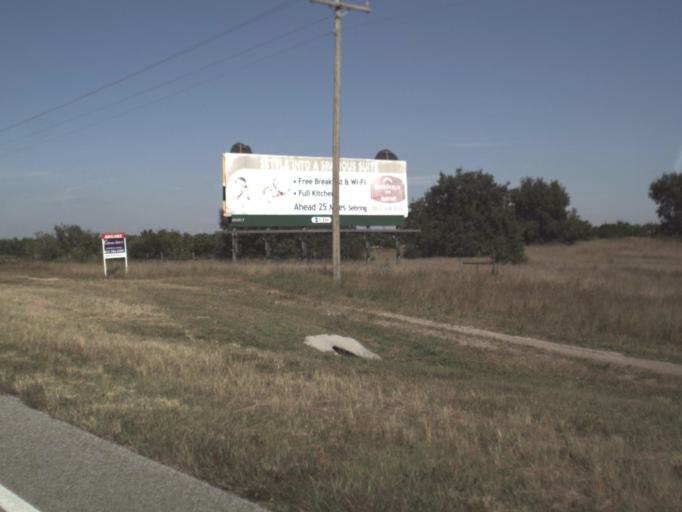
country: US
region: Florida
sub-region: Highlands County
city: Placid Lakes
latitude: 27.1892
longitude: -81.3285
